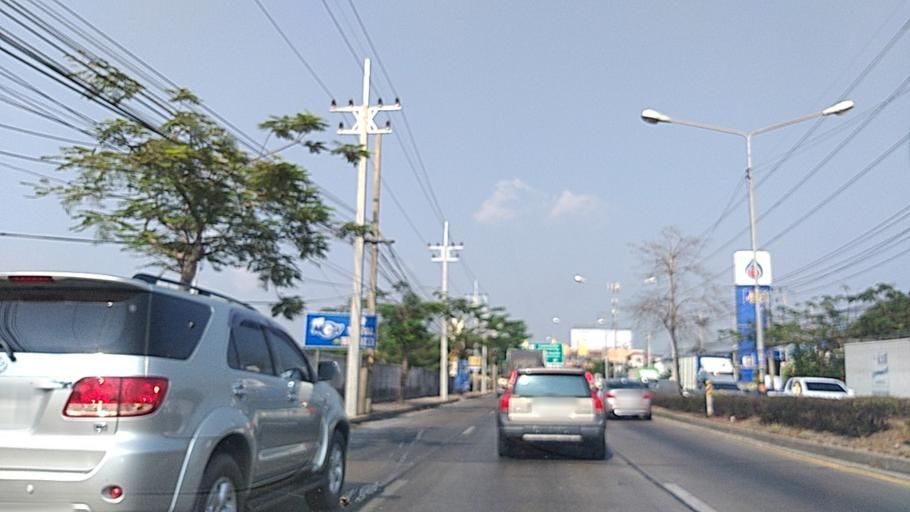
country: TH
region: Bangkok
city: Sai Mai
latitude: 13.9328
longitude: 100.6909
